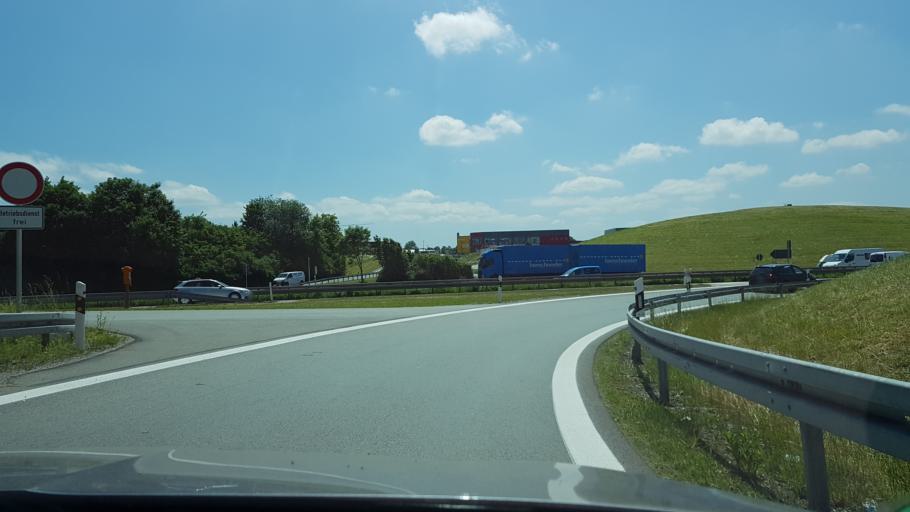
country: DE
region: Bavaria
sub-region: Upper Bavaria
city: Poing
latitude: 48.1501
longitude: 11.7881
